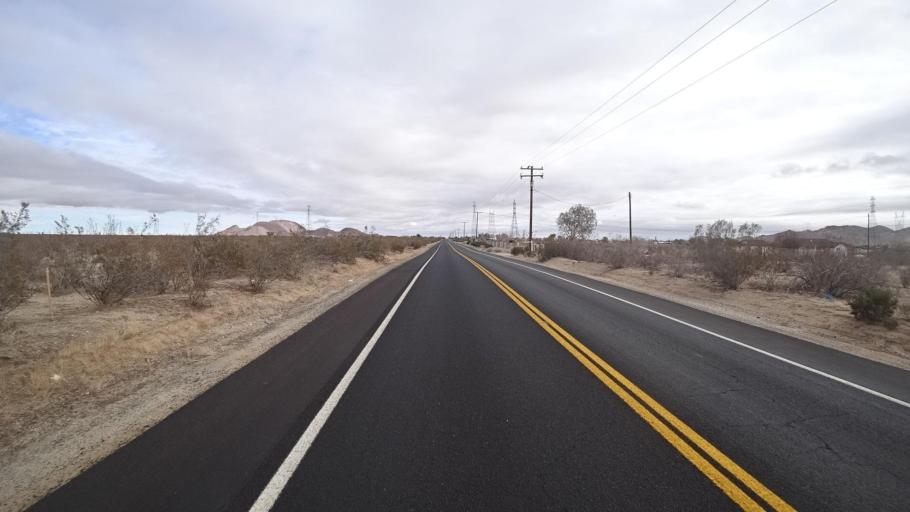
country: US
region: California
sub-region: Kern County
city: Rosamond
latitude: 34.9510
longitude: -118.2624
